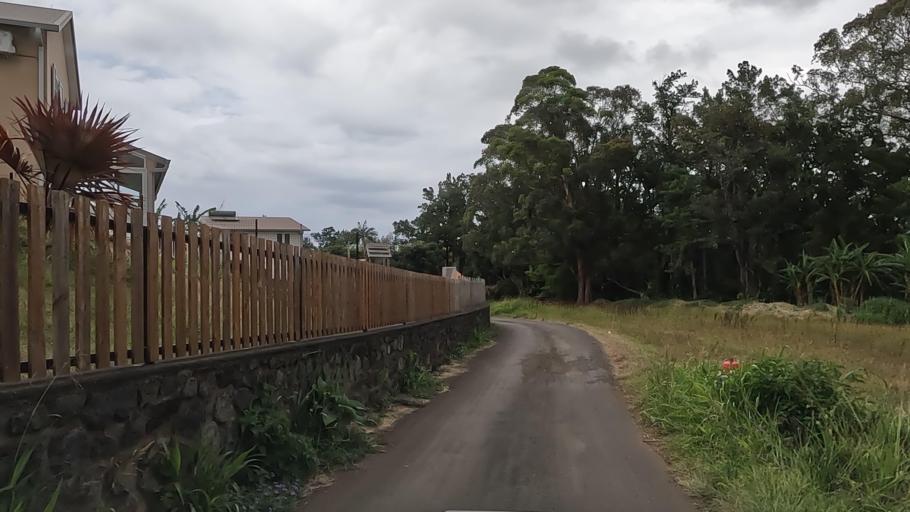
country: RE
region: Reunion
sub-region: Reunion
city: Le Tampon
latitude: -21.3121
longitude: 55.5352
